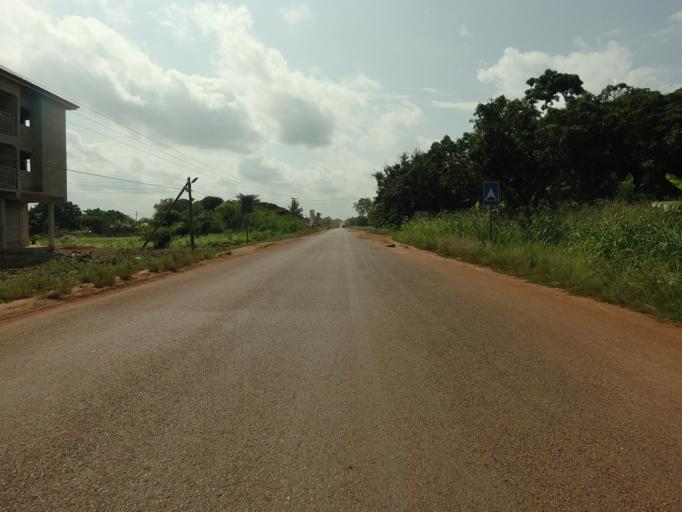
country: TG
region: Maritime
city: Tsevie
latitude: 6.3672
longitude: 0.8511
